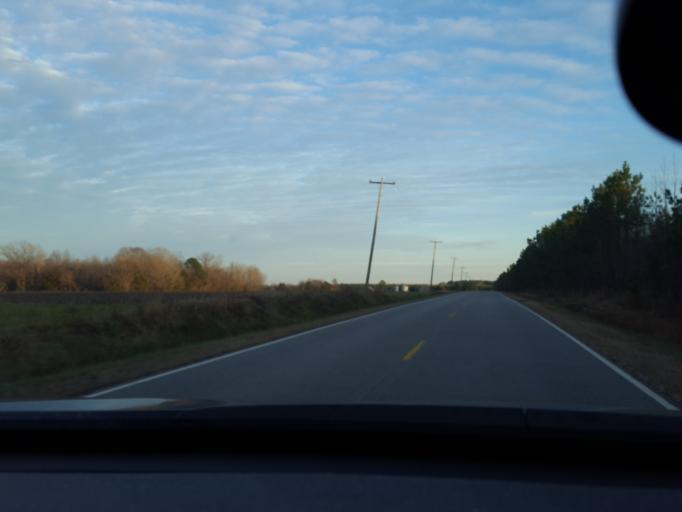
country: US
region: North Carolina
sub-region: Hertford County
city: Murfreesboro
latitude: 36.2799
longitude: -77.1630
